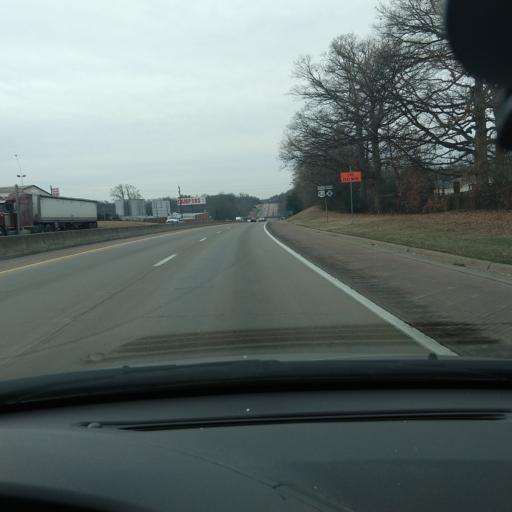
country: US
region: North Carolina
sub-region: Forsyth County
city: Winston-Salem
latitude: 36.0573
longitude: -80.2322
